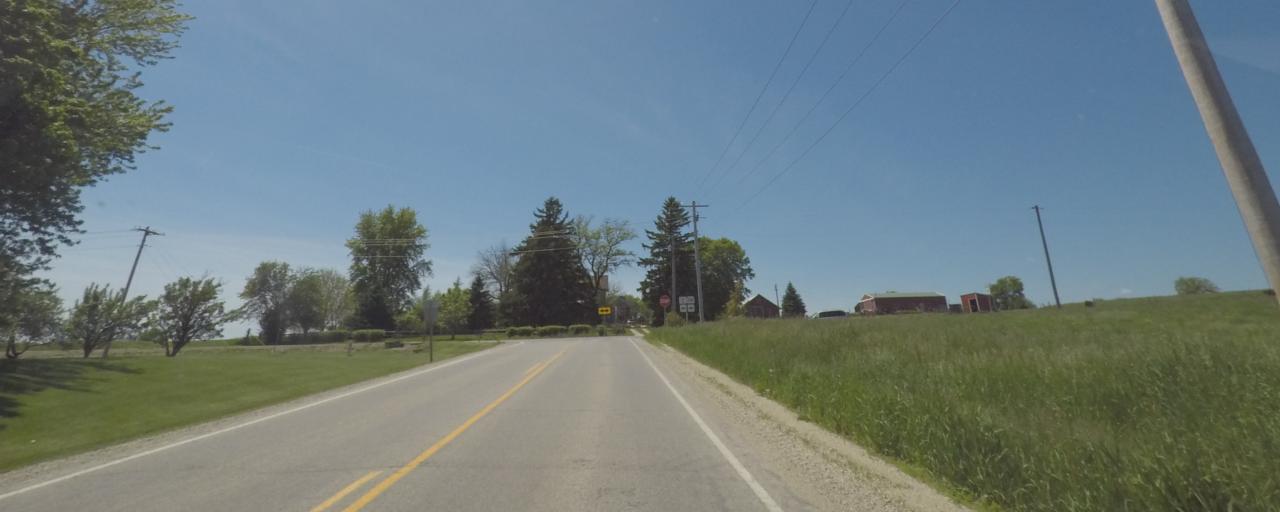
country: US
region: Wisconsin
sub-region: Green County
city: Brooklyn
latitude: 42.7872
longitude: -89.3684
